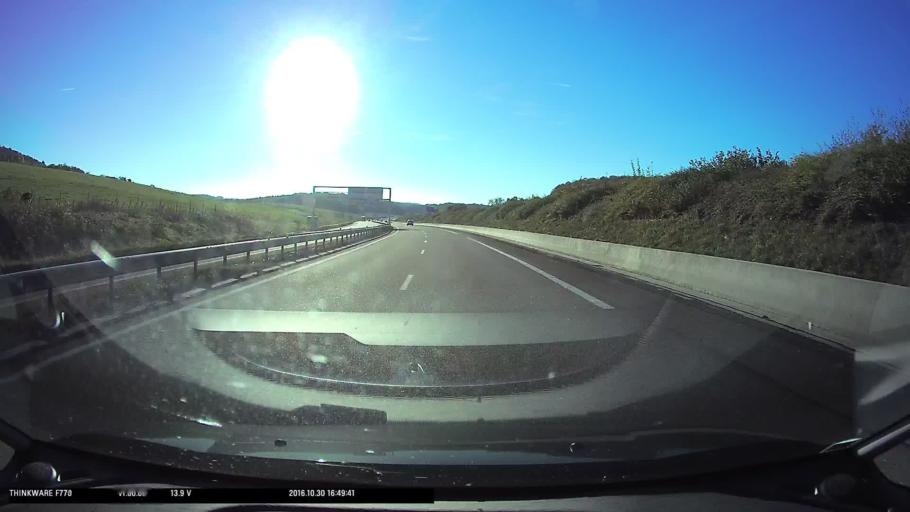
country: FR
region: Franche-Comte
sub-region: Departement du Doubs
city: Auxon-Dessous
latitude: 47.2772
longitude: 5.9477
